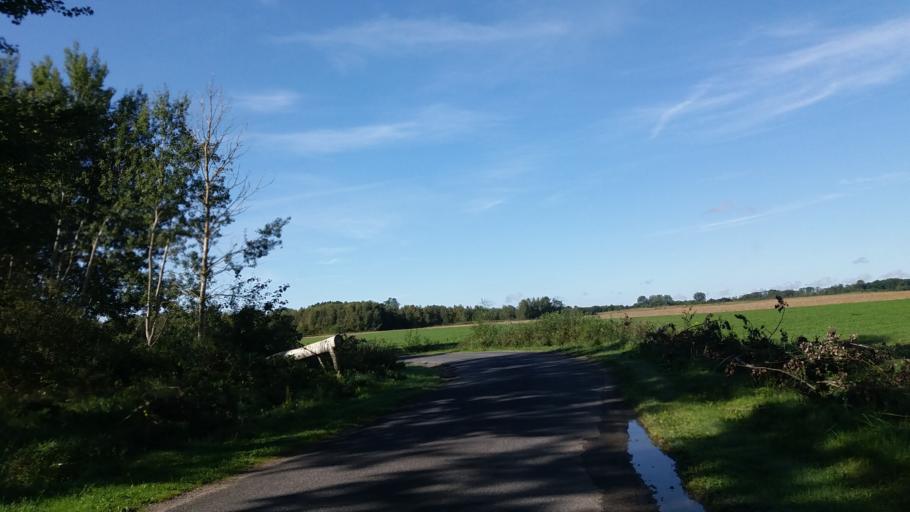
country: PL
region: West Pomeranian Voivodeship
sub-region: Powiat choszczenski
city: Choszczno
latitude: 53.1430
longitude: 15.4742
